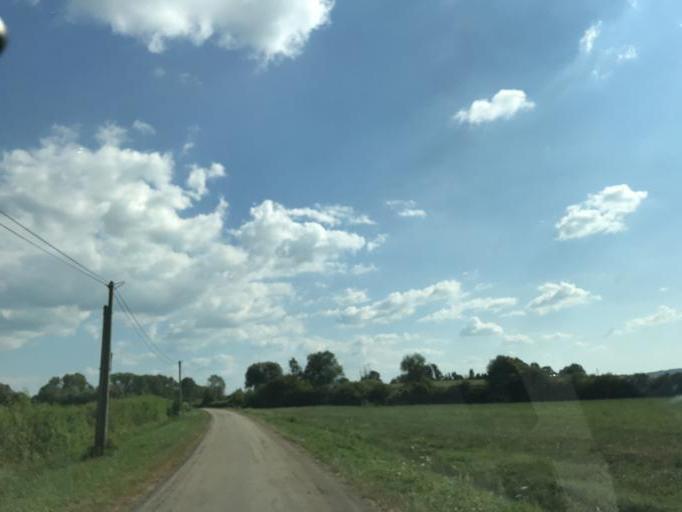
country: FR
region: Franche-Comte
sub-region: Departement du Jura
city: Clairvaux-les-Lacs
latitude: 46.5848
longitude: 5.7272
